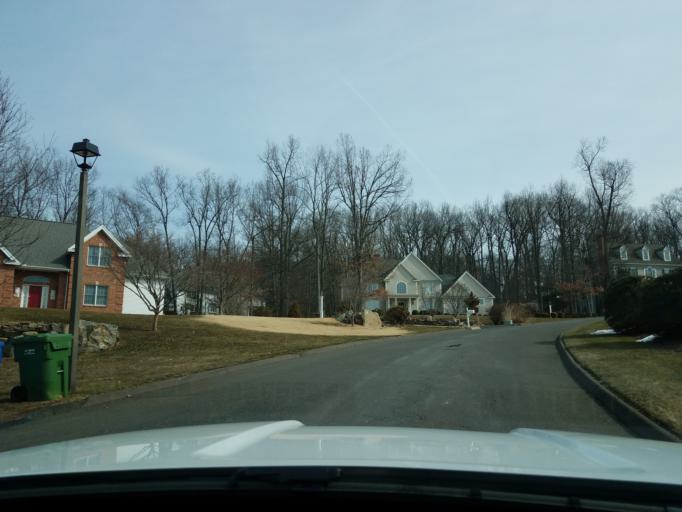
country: US
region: Connecticut
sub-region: Hartford County
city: Collinsville
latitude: 41.7850
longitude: -72.9036
